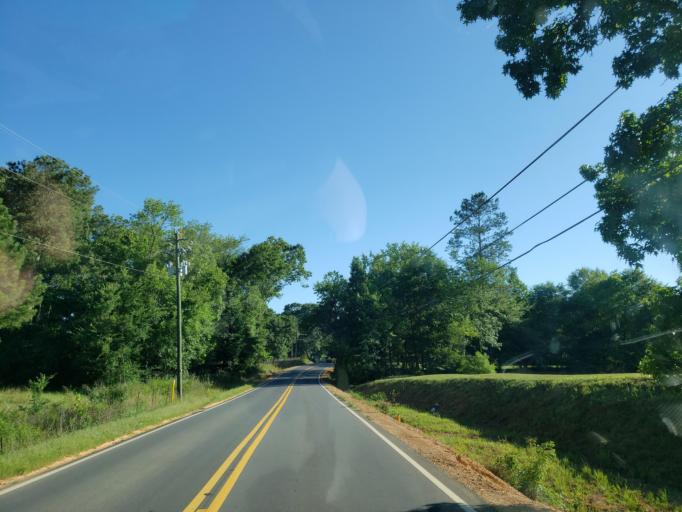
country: US
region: Georgia
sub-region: Floyd County
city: Shannon
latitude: 34.3422
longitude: -85.1502
